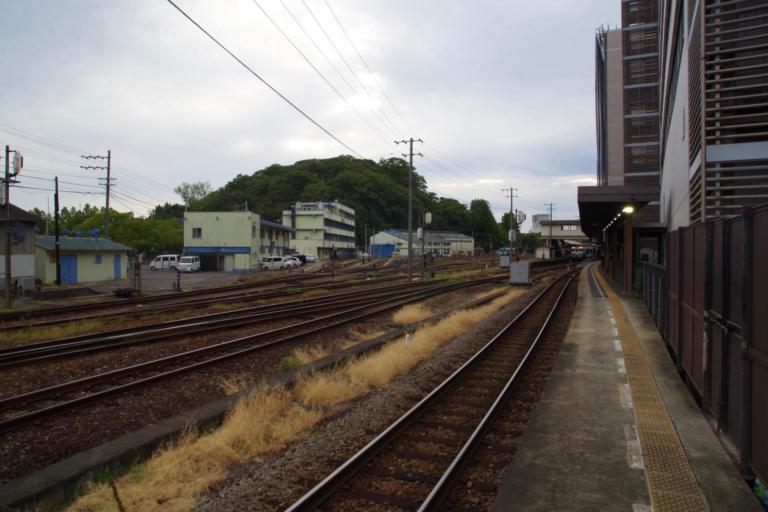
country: JP
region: Tokushima
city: Tokushima-shi
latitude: 34.0752
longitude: 134.5501
